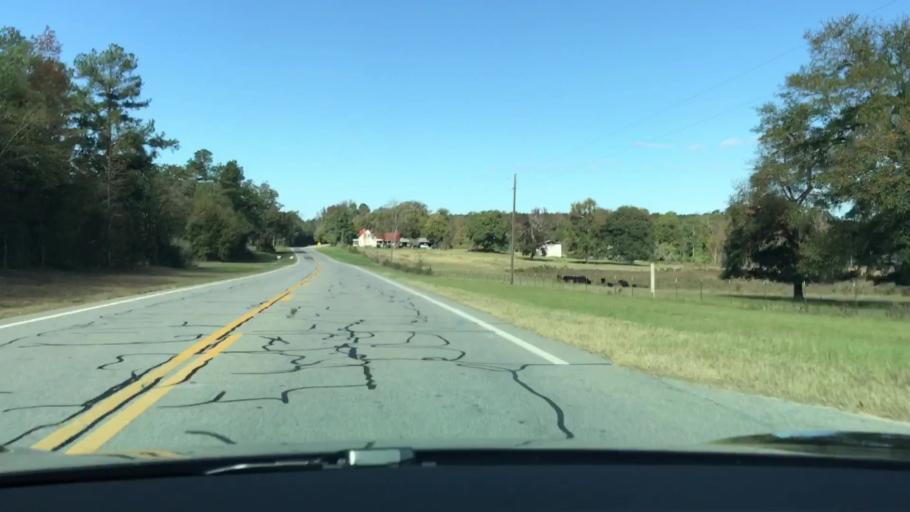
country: US
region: Georgia
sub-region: Warren County
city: Warrenton
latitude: 33.3431
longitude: -82.5768
